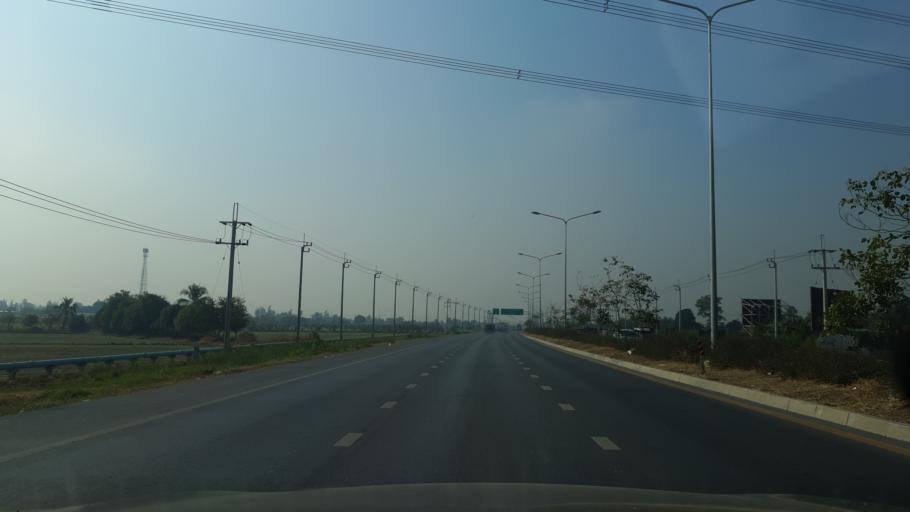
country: TH
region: Nonthaburi
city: Bang Bua Thong
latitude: 13.9695
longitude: 100.4630
